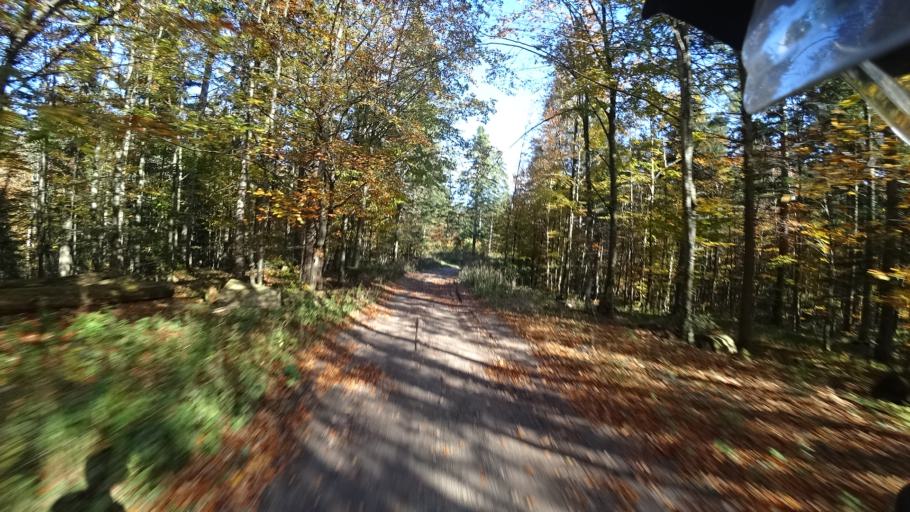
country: HR
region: Karlovacka
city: Plaski
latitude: 45.0250
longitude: 15.3693
